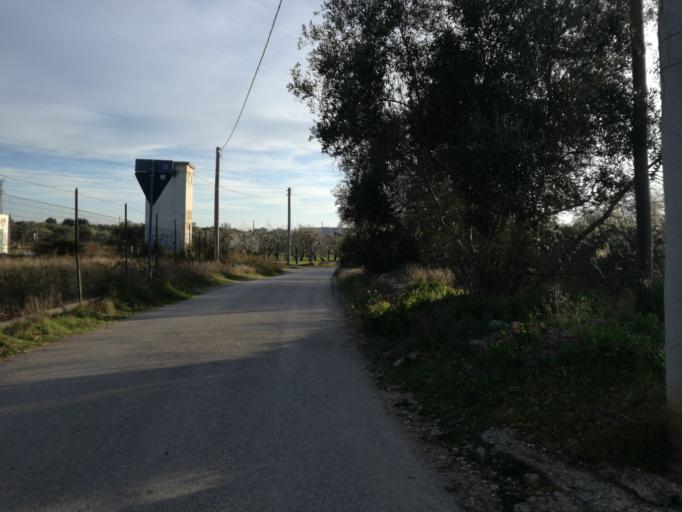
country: IT
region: Apulia
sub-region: Provincia di Bari
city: Valenzano
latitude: 41.0526
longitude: 16.8950
